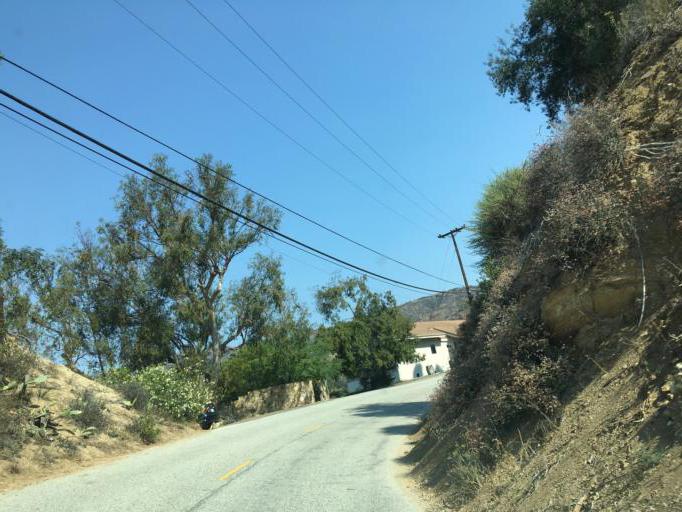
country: US
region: California
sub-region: Los Angeles County
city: Las Flores
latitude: 34.0438
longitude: -118.6473
